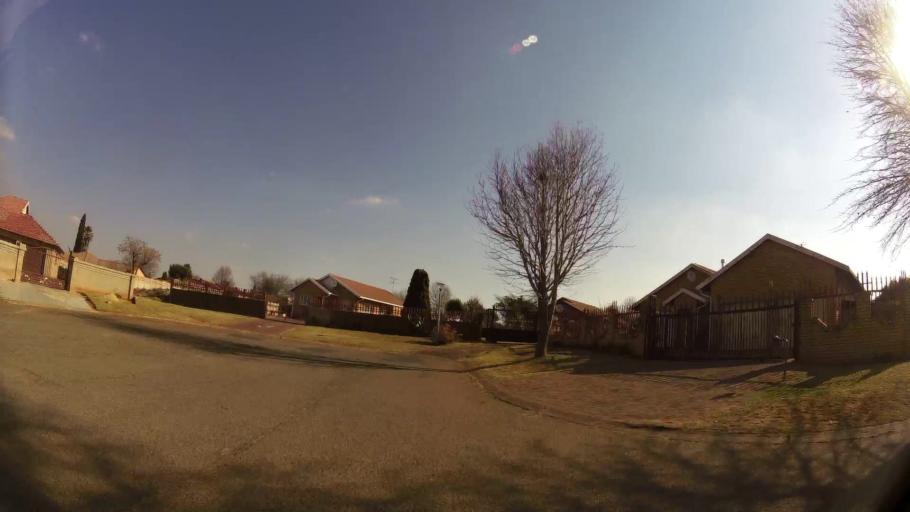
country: ZA
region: Gauteng
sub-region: Ekurhuleni Metropolitan Municipality
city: Brakpan
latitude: -26.2330
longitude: 28.3355
